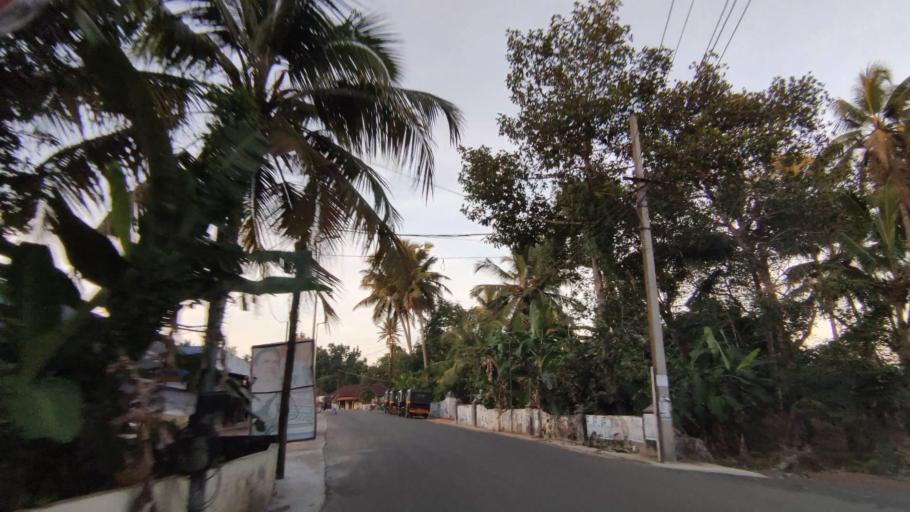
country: IN
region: Kerala
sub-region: Kottayam
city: Kottayam
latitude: 9.6408
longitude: 76.4967
